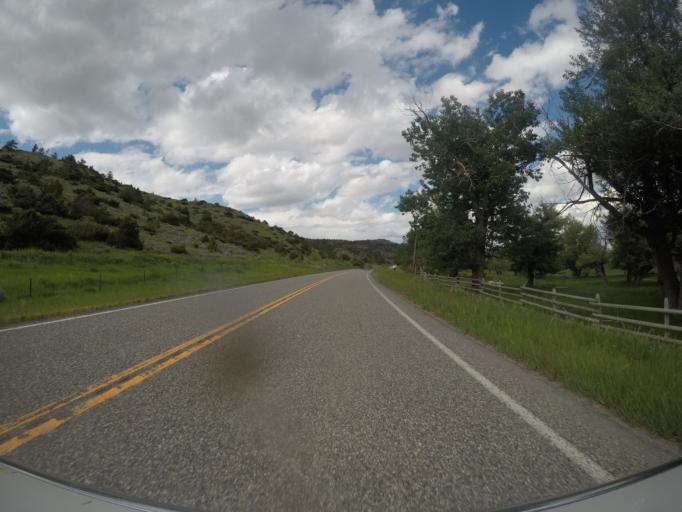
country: US
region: Montana
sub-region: Sweet Grass County
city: Big Timber
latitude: 45.6780
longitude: -110.0881
